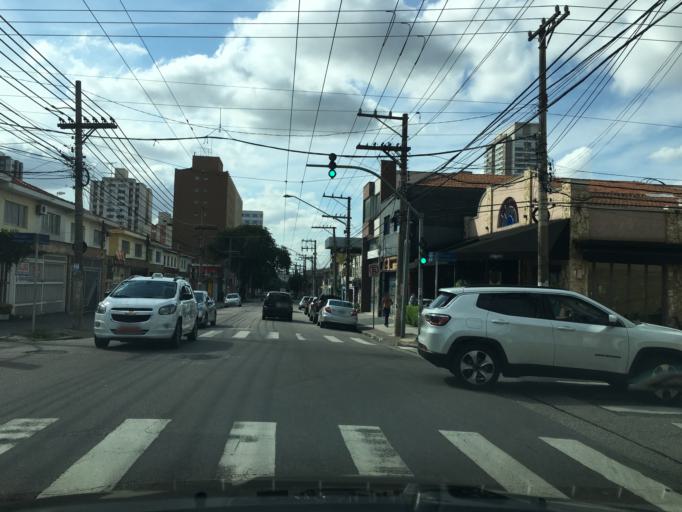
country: BR
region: Sao Paulo
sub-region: Sao Paulo
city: Sao Paulo
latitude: -23.5458
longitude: -46.5608
